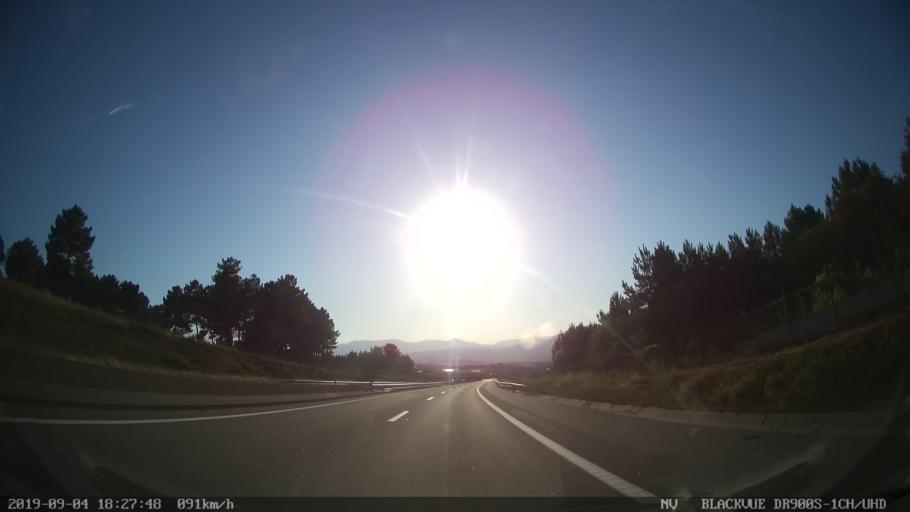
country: PT
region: Vila Real
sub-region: Vila Real
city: Vila Real
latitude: 41.2864
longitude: -7.7048
